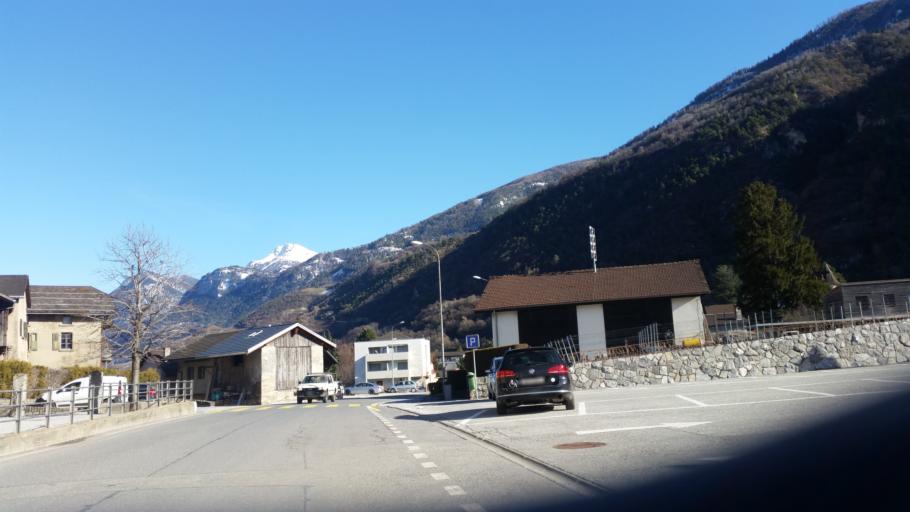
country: CH
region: Valais
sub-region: Sierre District
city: Grone
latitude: 46.2515
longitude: 7.4541
